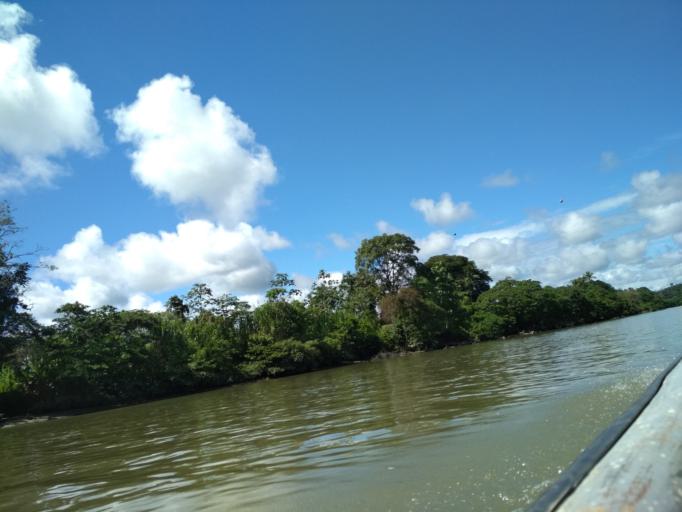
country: CO
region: Cauca
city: Timbiqui
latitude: 2.7676
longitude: -77.6631
